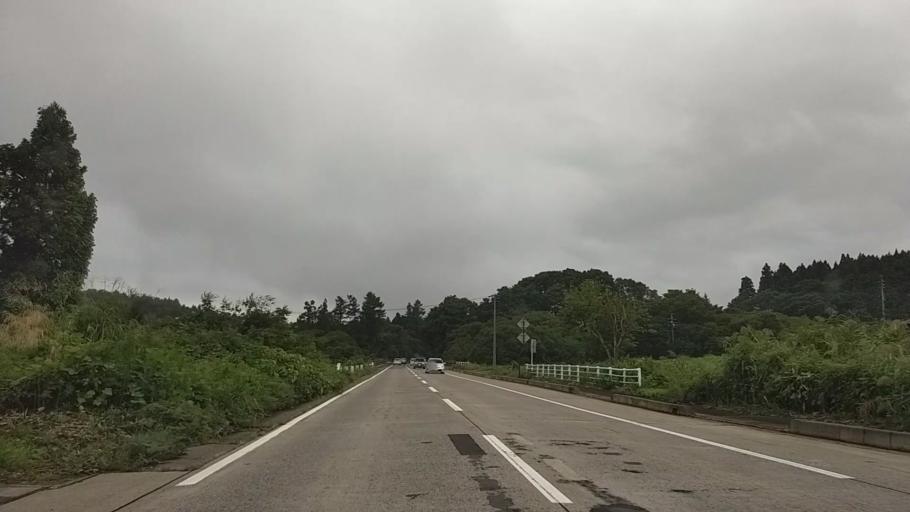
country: JP
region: Nagano
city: Iiyama
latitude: 36.8185
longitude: 138.3447
